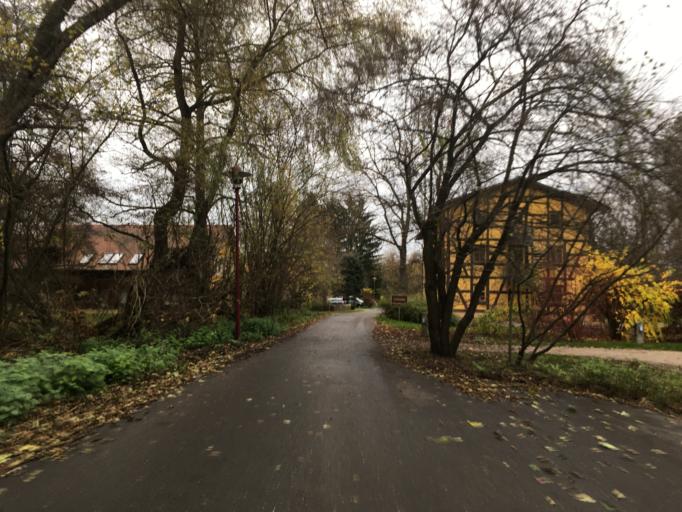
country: DE
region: Brandenburg
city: Mullrose
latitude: 52.2449
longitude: 14.4522
